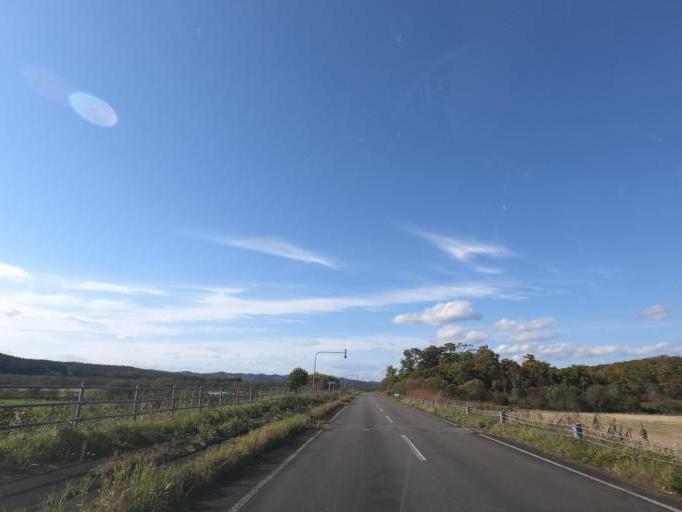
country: JP
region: Hokkaido
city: Obihiro
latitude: 42.6327
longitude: 143.5210
